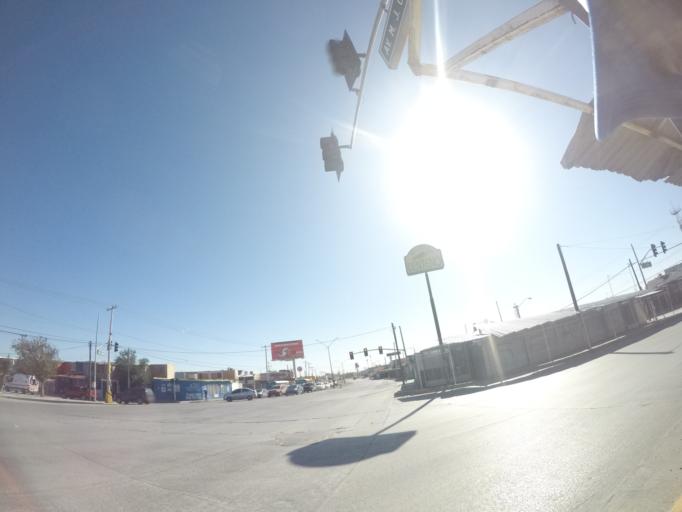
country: US
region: Texas
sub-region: El Paso County
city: Socorro
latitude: 31.6656
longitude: -106.4015
